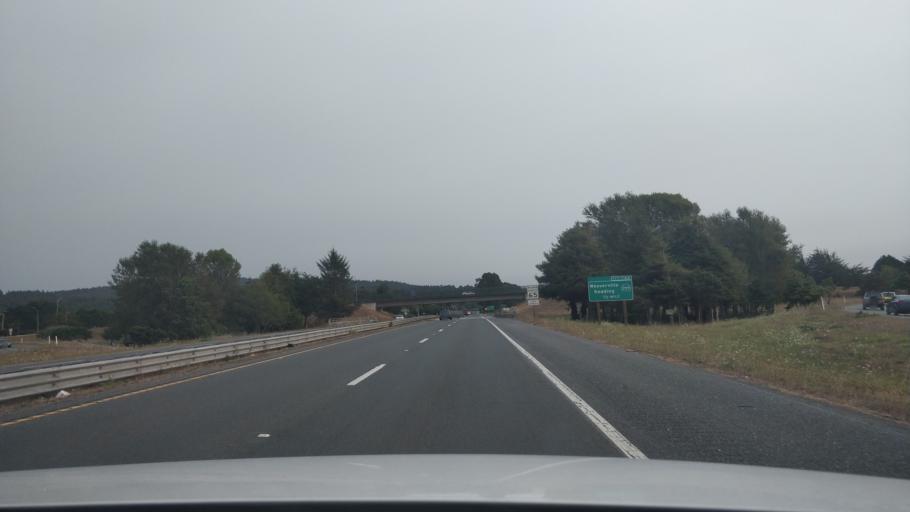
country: US
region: California
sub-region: Humboldt County
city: Arcata
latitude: 40.9068
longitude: -124.0881
